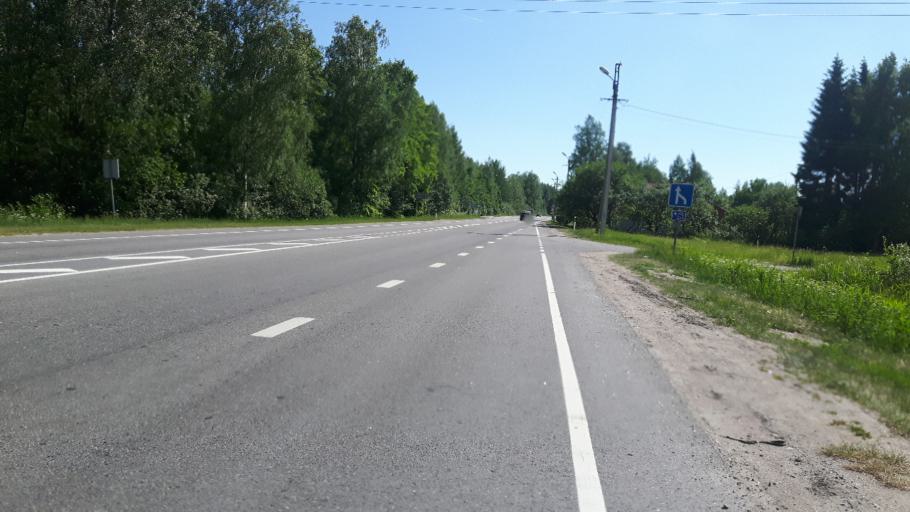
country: EE
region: Paernumaa
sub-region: Paikuse vald
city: Paikuse
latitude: 58.3892
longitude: 24.6409
